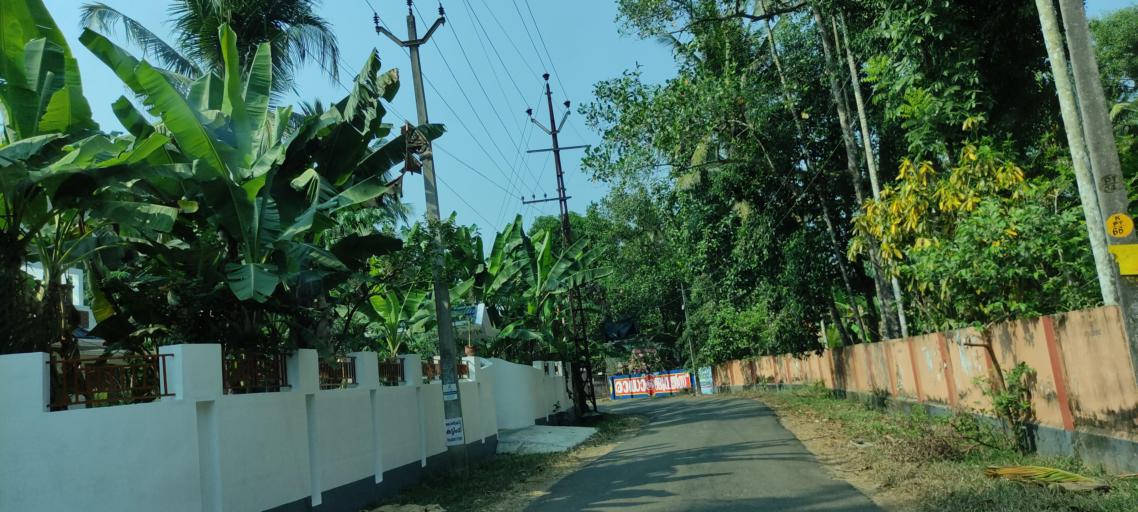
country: IN
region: Kerala
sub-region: Pattanamtitta
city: Tiruvalla
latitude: 9.3584
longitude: 76.5152
